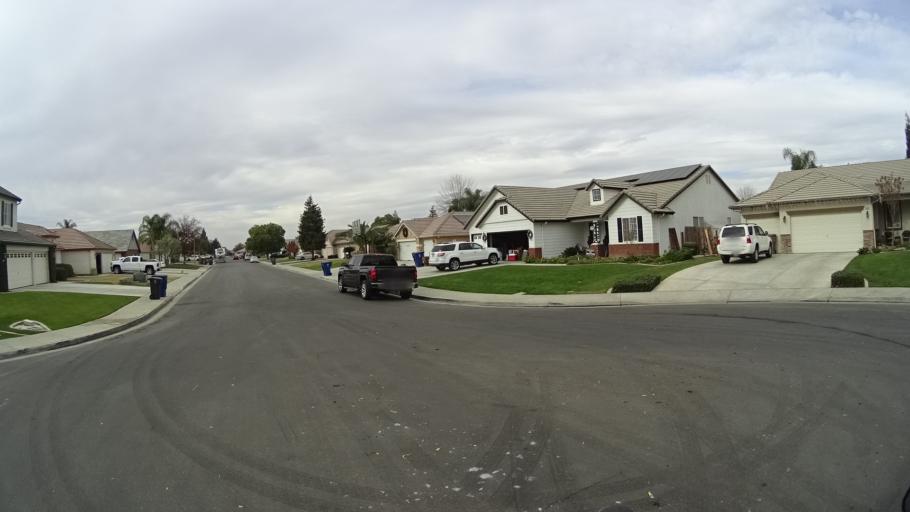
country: US
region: California
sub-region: Kern County
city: Rosedale
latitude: 35.4203
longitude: -119.1284
